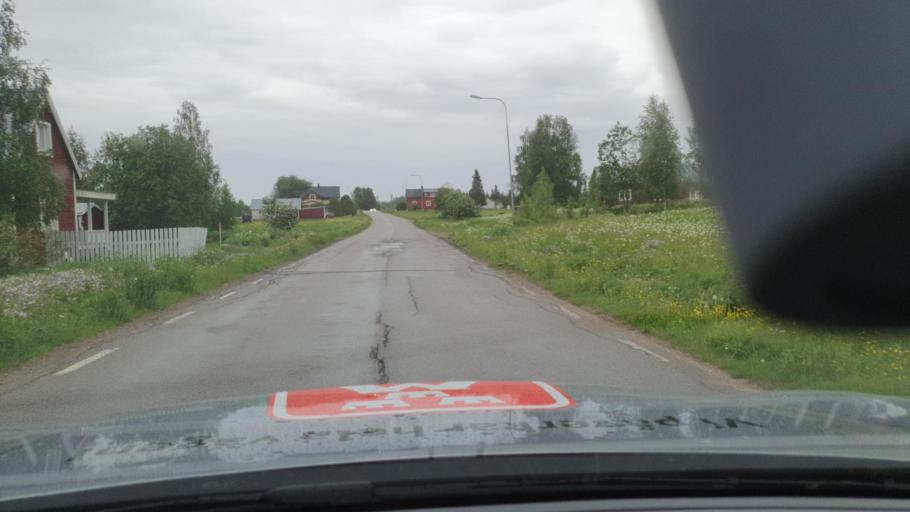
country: SE
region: Norrbotten
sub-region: Pajala Kommun
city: Pajala
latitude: 66.7968
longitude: 23.1242
